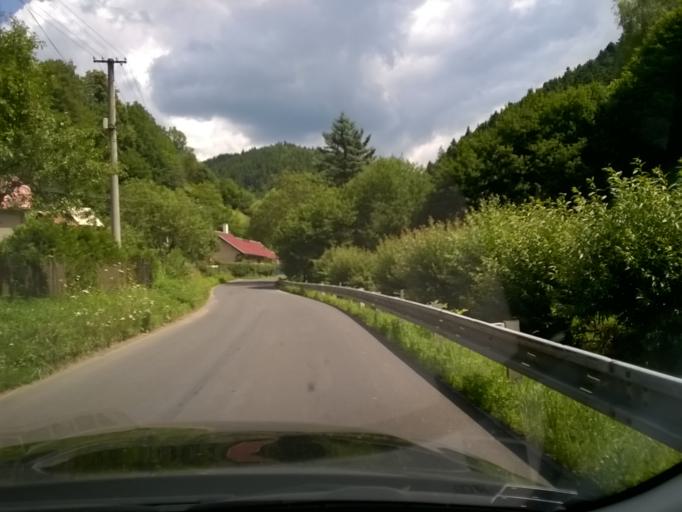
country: SK
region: Banskobystricky
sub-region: Okres Banska Bystrica
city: Banska Stiavnica
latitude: 48.4590
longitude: 18.8156
